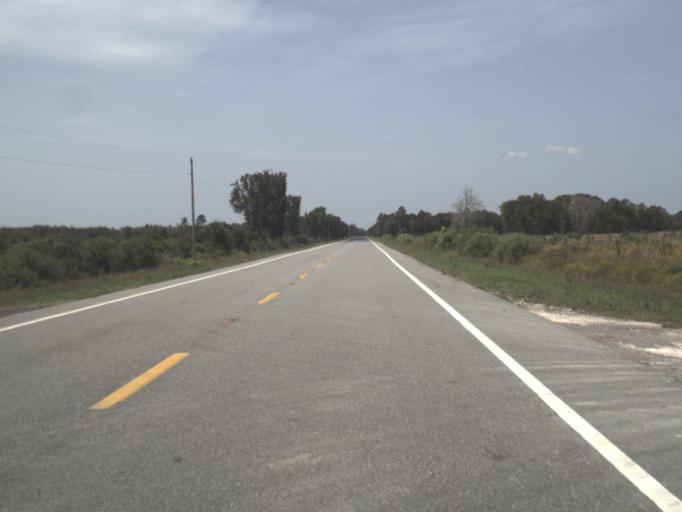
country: US
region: Florida
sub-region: Taylor County
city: Steinhatchee
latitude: 29.8062
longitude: -83.3186
